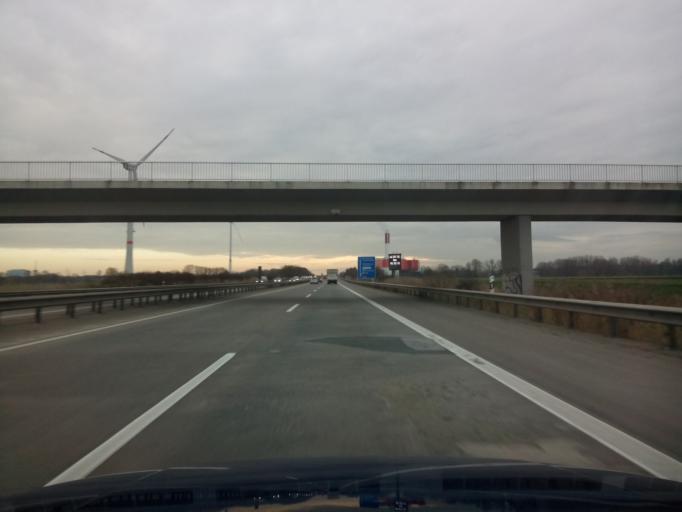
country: DE
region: Lower Saxony
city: Schiffdorf
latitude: 53.5566
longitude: 8.6195
